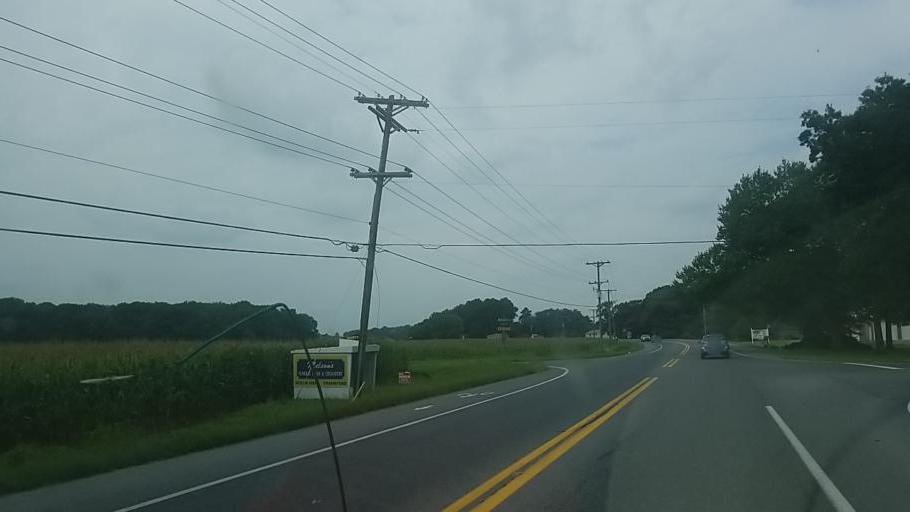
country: US
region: Delaware
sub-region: Sussex County
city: Long Neck
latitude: 38.5568
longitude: -75.1634
